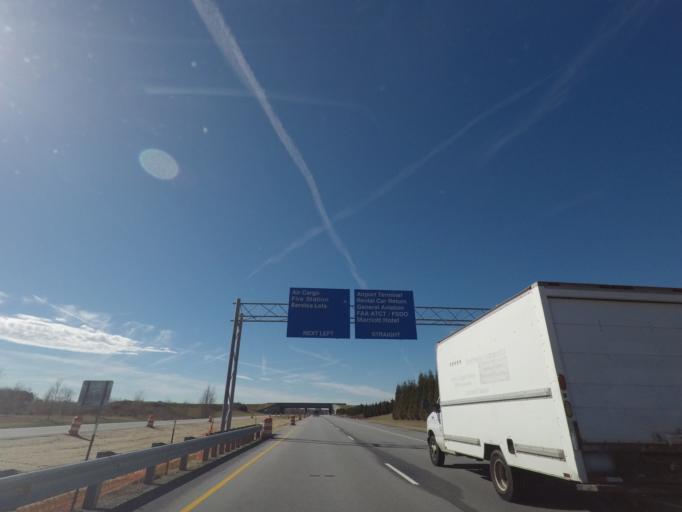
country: US
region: North Carolina
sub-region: Guilford County
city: Oak Ridge
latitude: 36.1167
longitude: -79.9342
